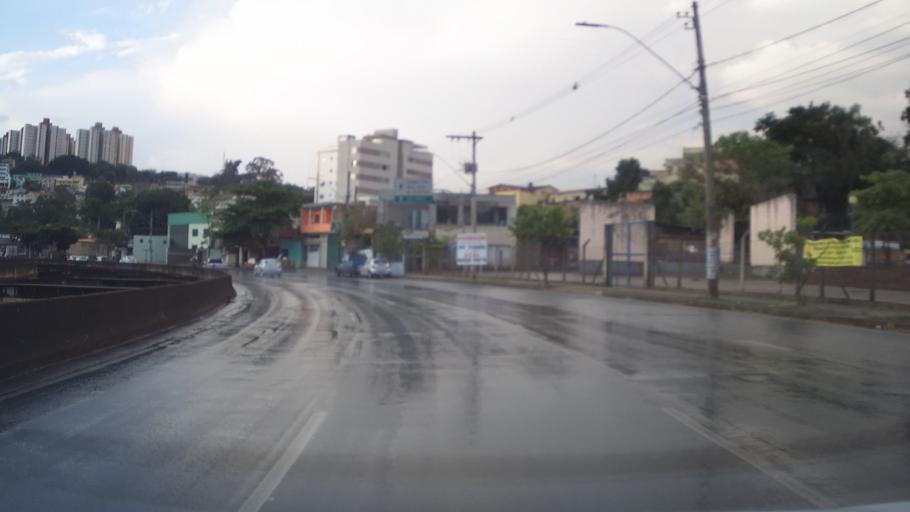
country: BR
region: Minas Gerais
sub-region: Belo Horizonte
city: Belo Horizonte
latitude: -19.9449
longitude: -43.9871
